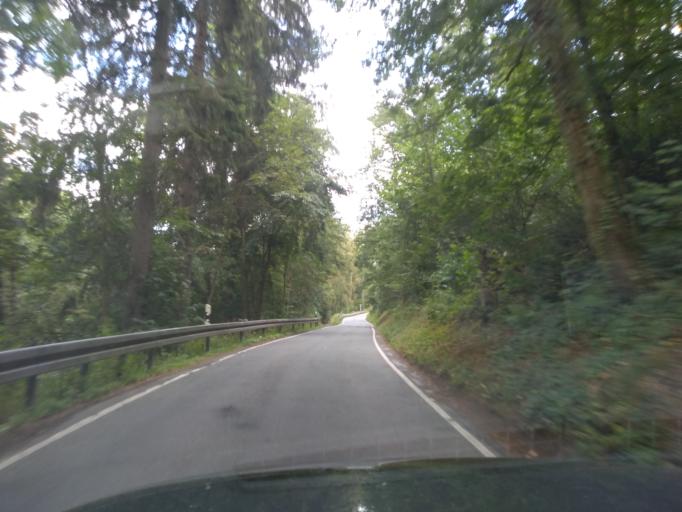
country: DE
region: North Rhine-Westphalia
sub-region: Regierungsbezirk Arnsberg
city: Luedenscheid
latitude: 51.2332
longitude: 7.5844
